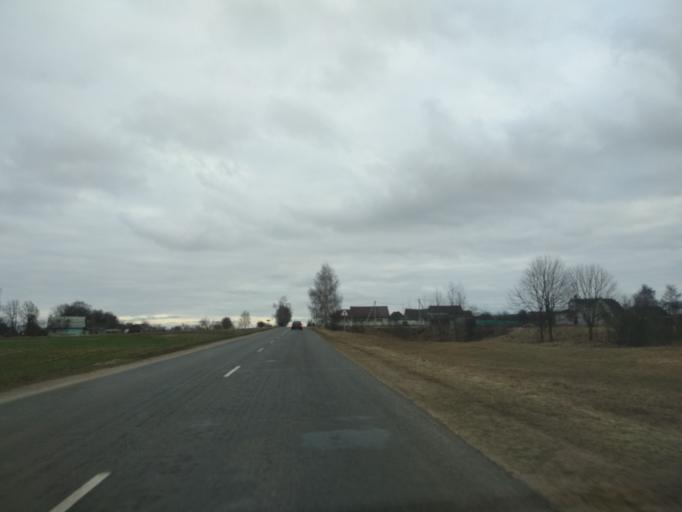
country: BY
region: Minsk
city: Svislach
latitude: 53.5688
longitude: 28.0040
